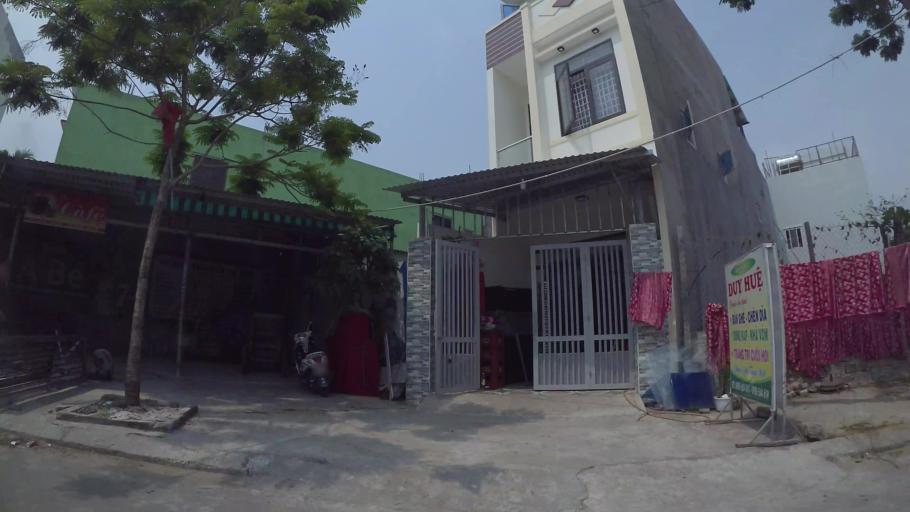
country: VN
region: Da Nang
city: Son Tra
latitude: 16.1017
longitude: 108.2548
